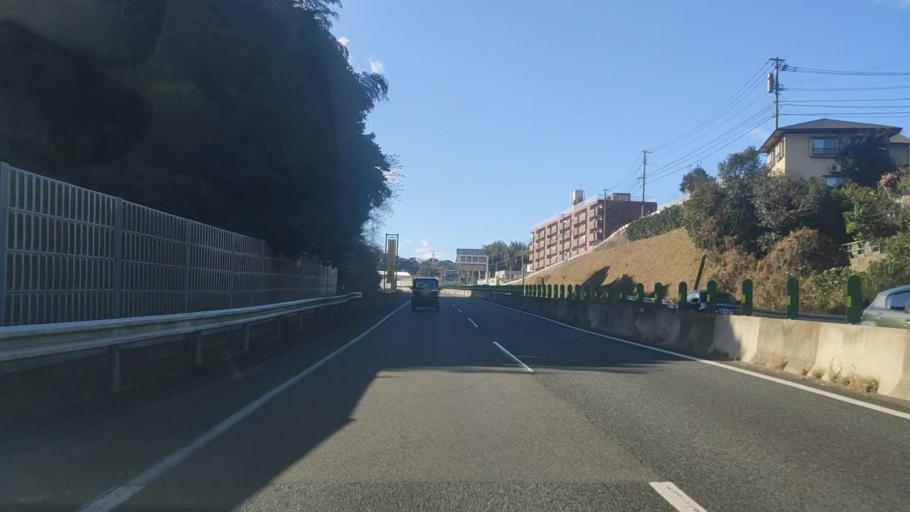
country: JP
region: Fukuoka
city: Kitakyushu
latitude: 33.8638
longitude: 130.8568
